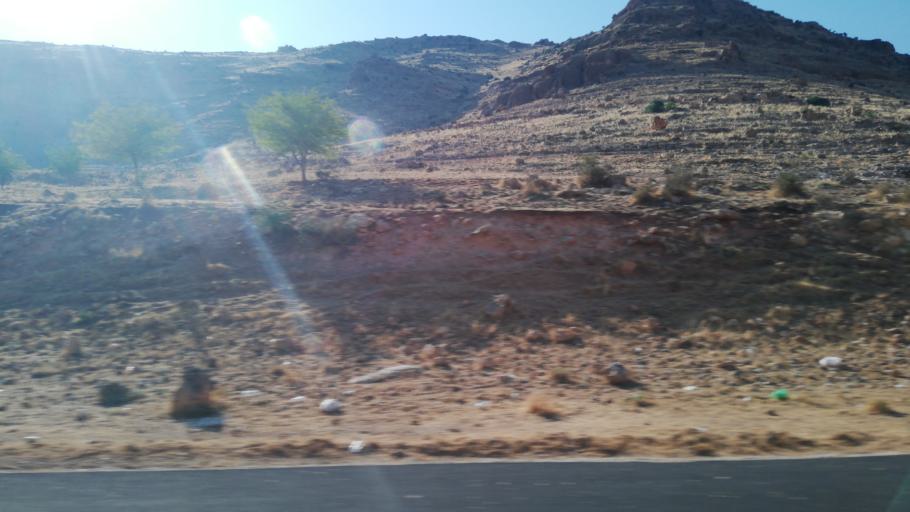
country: TR
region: Mardin
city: Sivrice
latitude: 37.2316
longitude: 41.3314
